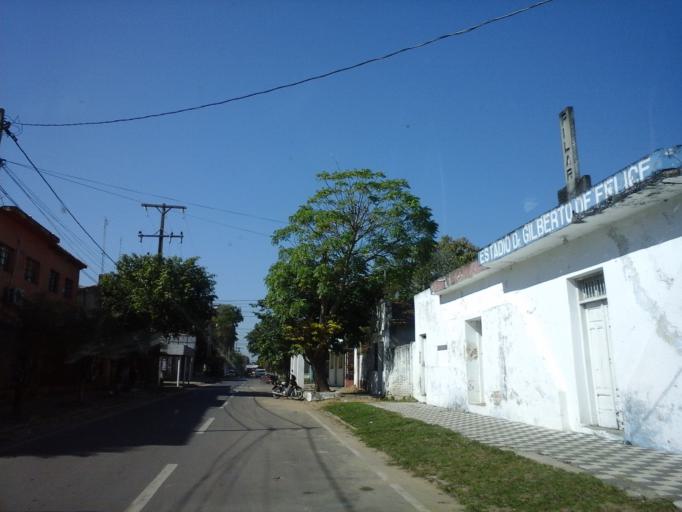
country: PY
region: Neembucu
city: Pilar
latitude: -26.8568
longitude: -58.3096
